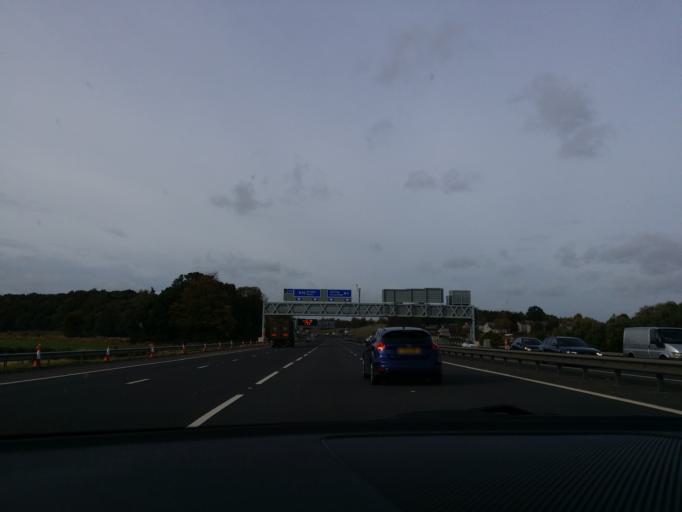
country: GB
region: Scotland
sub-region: Edinburgh
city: Kirkliston
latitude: 55.9490
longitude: -3.4103
